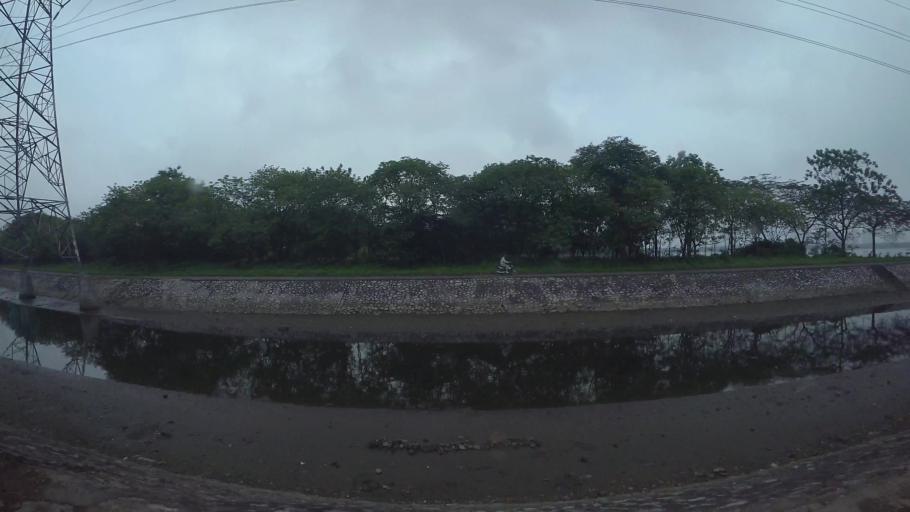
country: VN
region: Ha Noi
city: Van Dien
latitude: 20.9756
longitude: 105.8587
